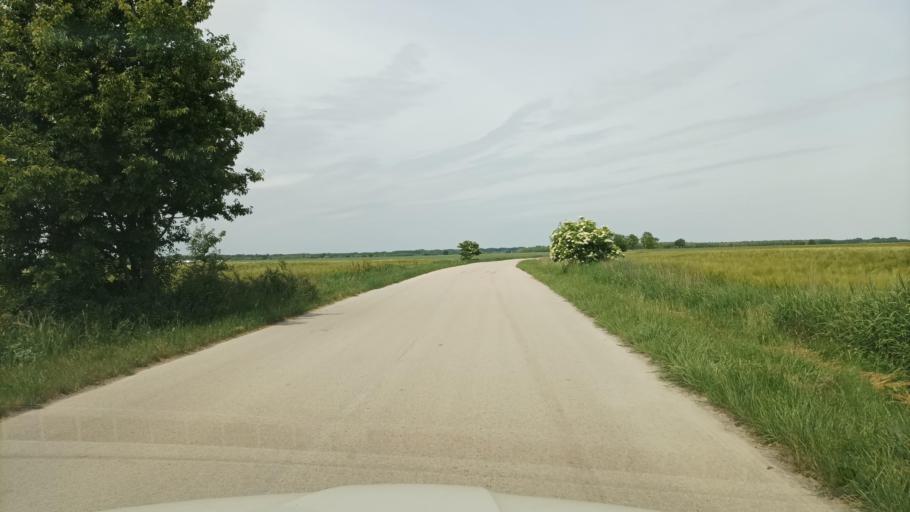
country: HU
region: Pest
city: Rackeve
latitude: 47.1116
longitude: 18.9225
